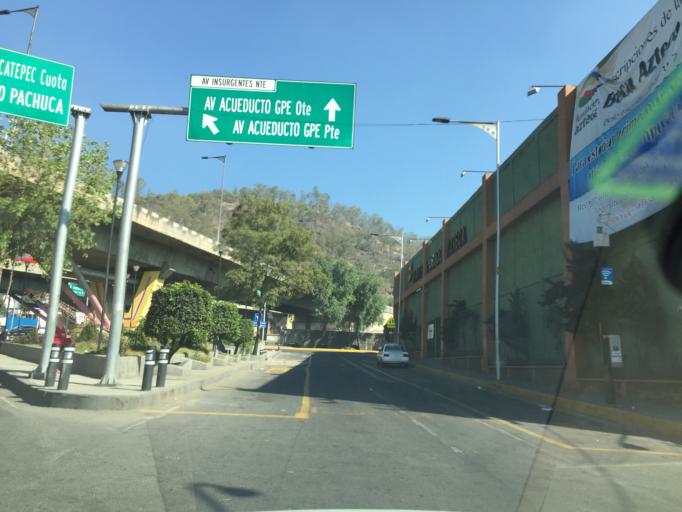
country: MX
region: Mexico
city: Colonia Lindavista
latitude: 19.5010
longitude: -99.1175
